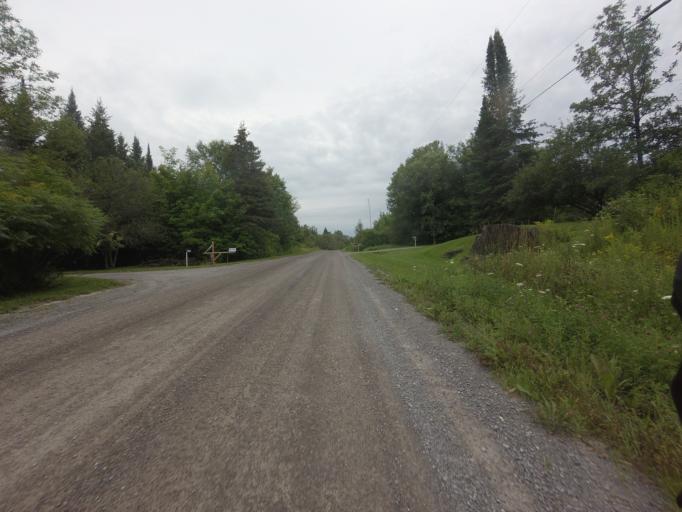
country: CA
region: Ontario
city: Carleton Place
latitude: 45.1613
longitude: -76.2699
